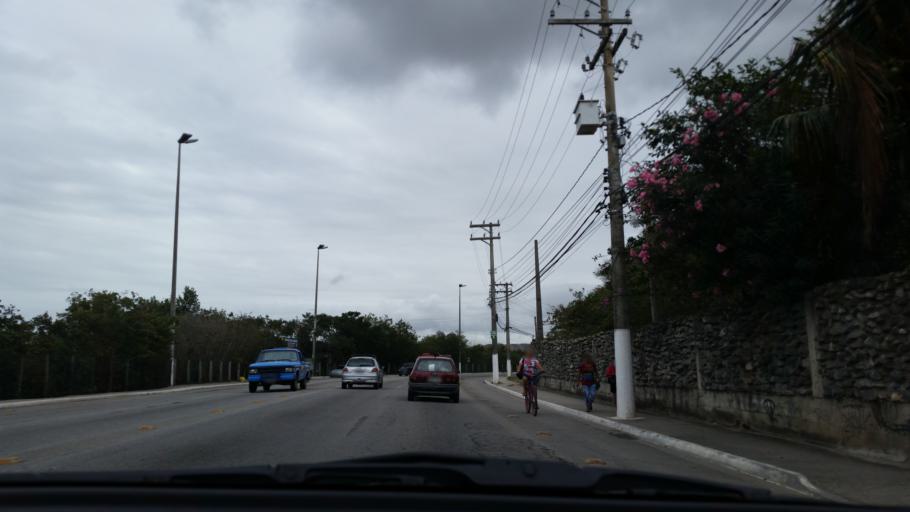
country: BR
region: Rio de Janeiro
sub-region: Cabo Frio
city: Cabo Frio
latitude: -22.8654
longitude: -42.0320
